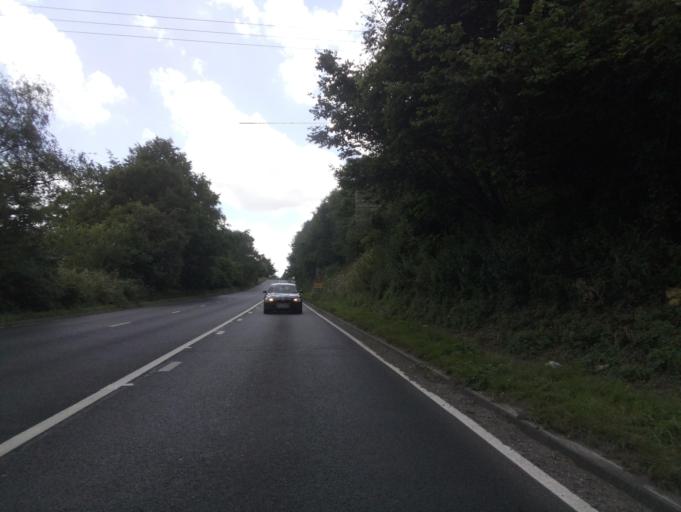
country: GB
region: England
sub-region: Borough of Swindon
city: Chiseldon
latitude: 51.5240
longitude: -1.7248
